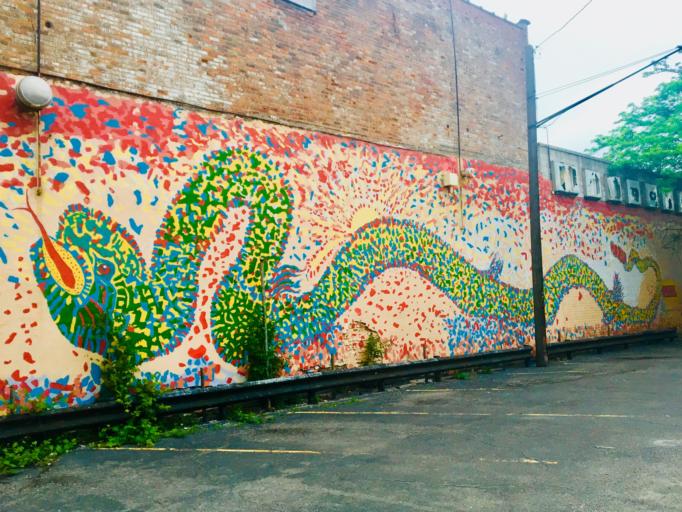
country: US
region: Michigan
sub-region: Wayne County
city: River Rouge
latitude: 42.3127
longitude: -83.1251
